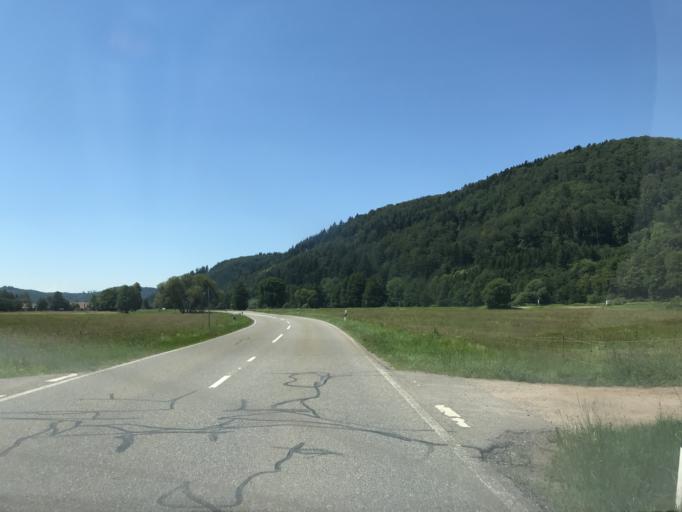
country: DE
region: Baden-Wuerttemberg
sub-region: Freiburg Region
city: Schopfheim
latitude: 47.6744
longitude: 7.8050
